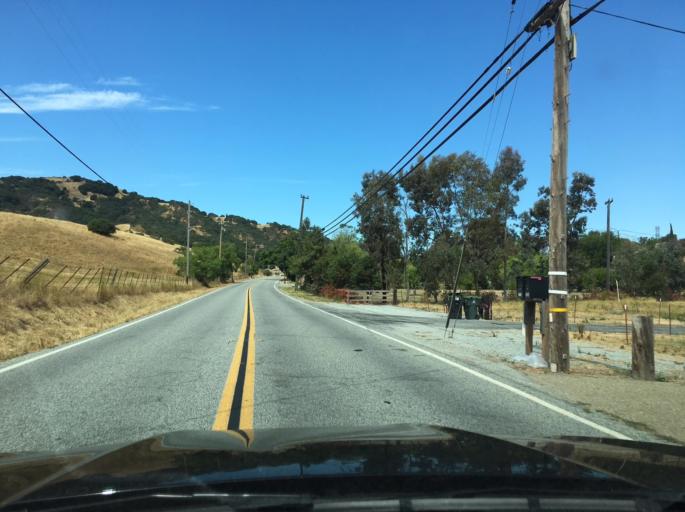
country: US
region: California
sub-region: Santa Clara County
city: Seven Trees
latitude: 37.1880
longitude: -121.7881
